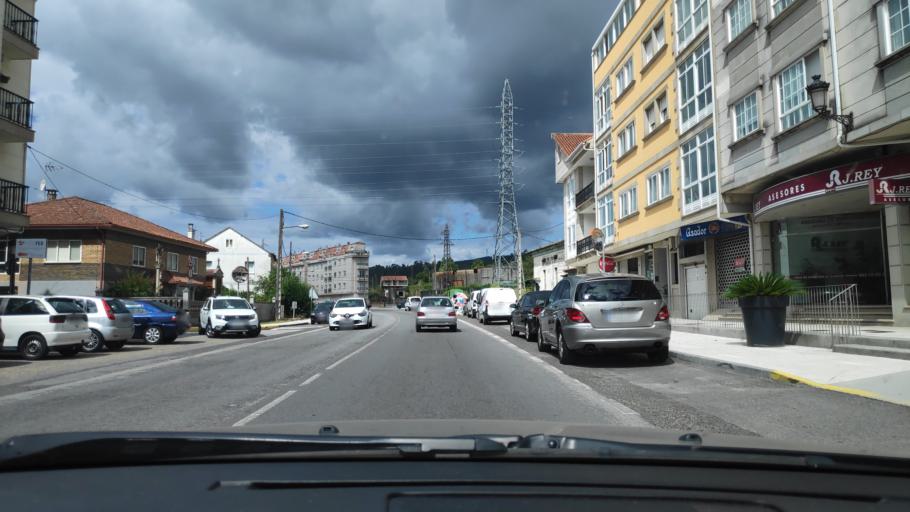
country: ES
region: Galicia
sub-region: Provincia de Pontevedra
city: Caldas de Reis
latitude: 42.6042
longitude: -8.6479
